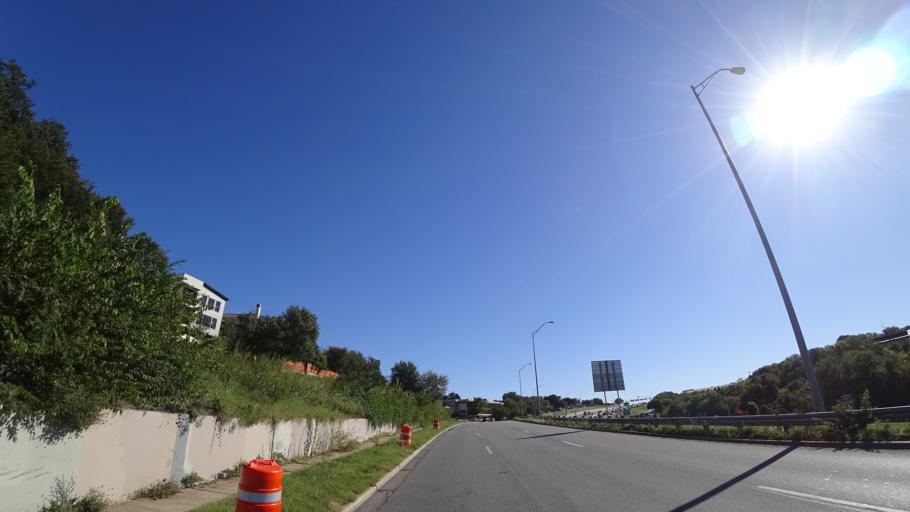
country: US
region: Texas
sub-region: Travis County
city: Austin
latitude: 30.2465
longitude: -97.7346
